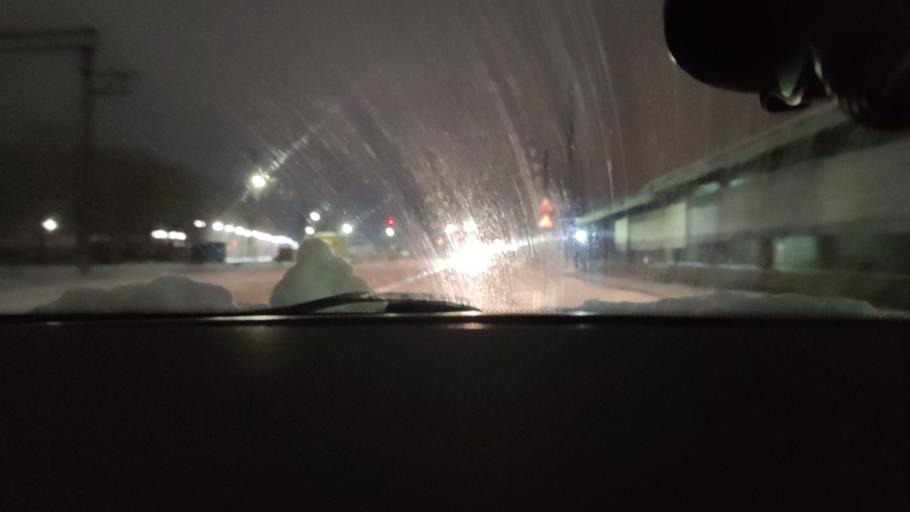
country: RU
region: Perm
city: Krasnokamsk
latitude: 58.0728
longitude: 55.7760
